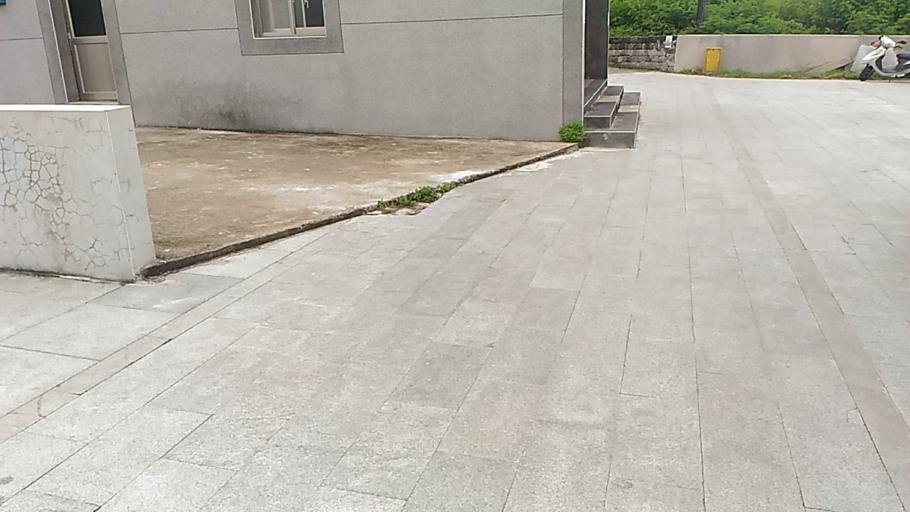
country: TW
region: Taiwan
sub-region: Penghu
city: Ma-kung
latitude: 23.3702
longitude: 119.4951
